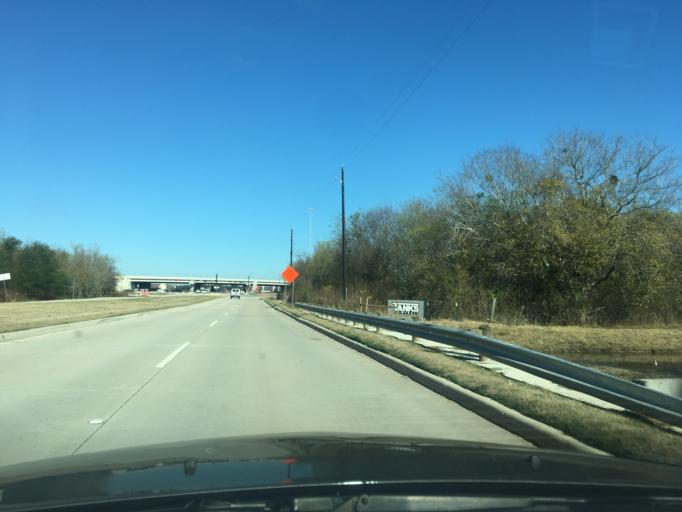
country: US
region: Texas
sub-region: Fort Bend County
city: Greatwood
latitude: 29.5528
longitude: -95.7186
